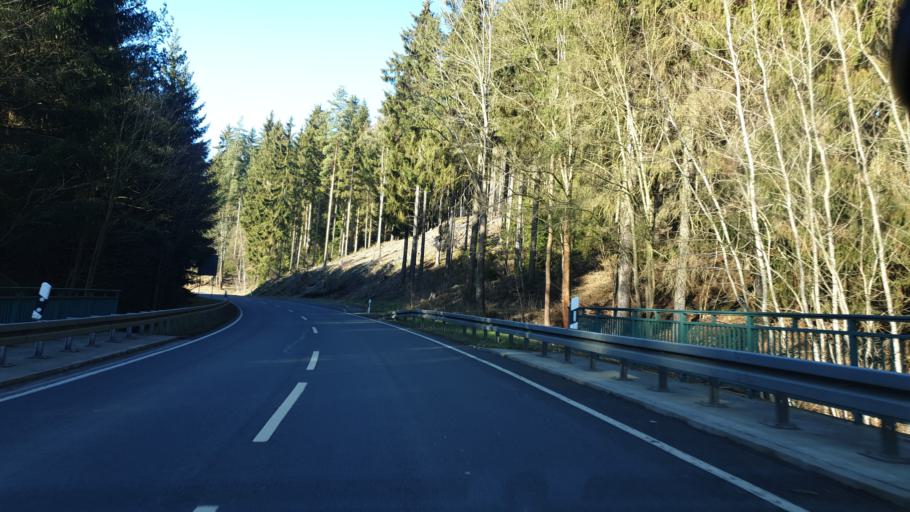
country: DE
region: Saxony
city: Markneukirchen
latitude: 50.2768
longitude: 12.2921
